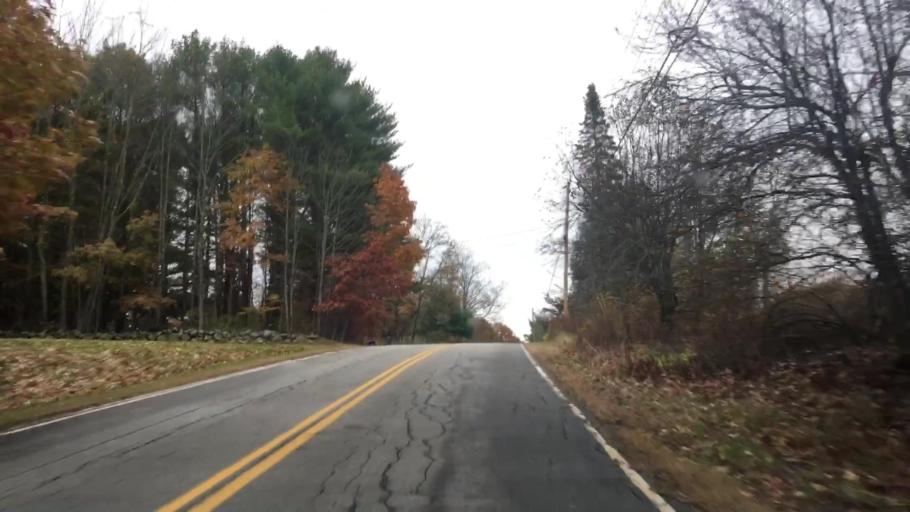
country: US
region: Maine
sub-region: Lincoln County
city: Whitefield
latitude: 44.1706
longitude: -69.6637
